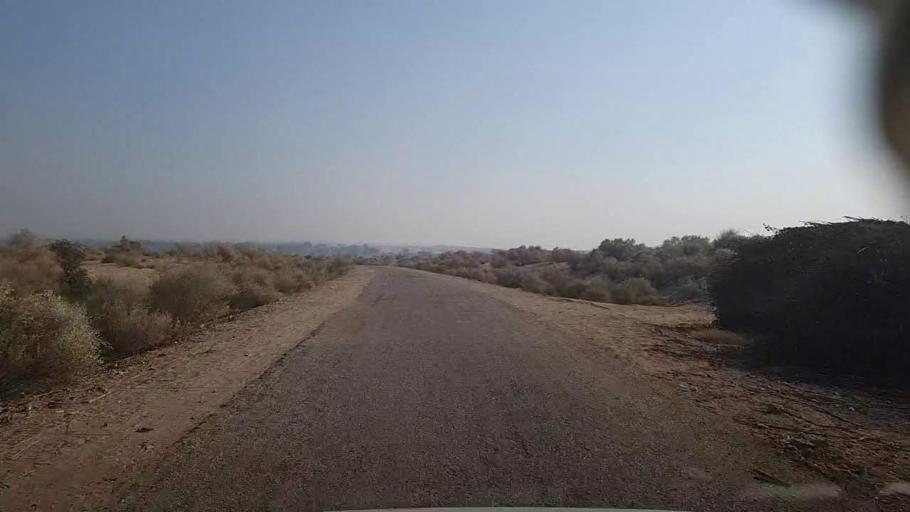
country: PK
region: Sindh
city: Kandiari
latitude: 26.8237
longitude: 68.4894
